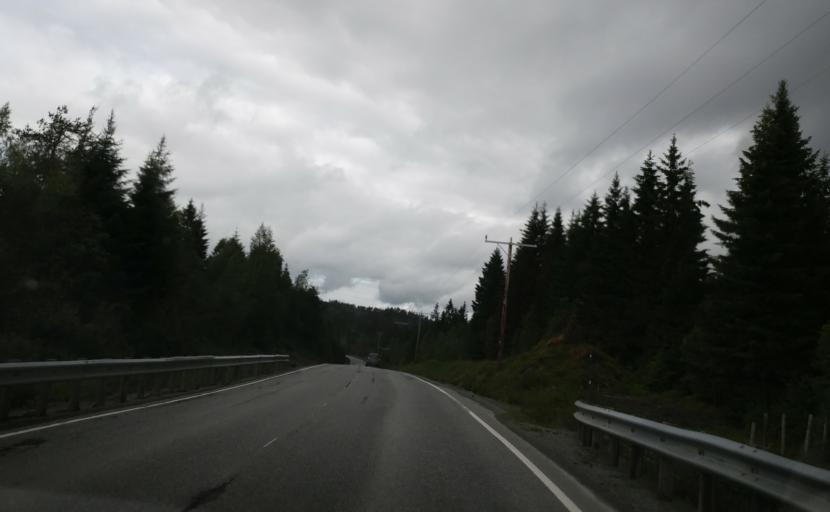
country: NO
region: Sor-Trondelag
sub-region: Selbu
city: Mebonden
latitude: 63.3490
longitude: 11.0786
